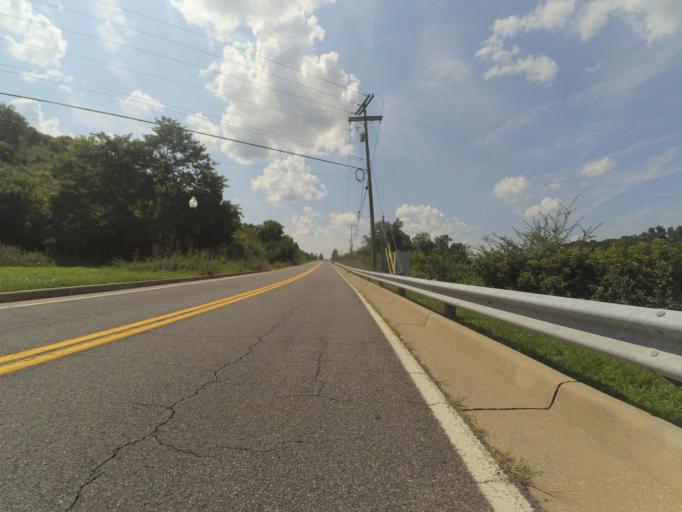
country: US
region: West Virginia
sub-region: Cabell County
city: Huntington
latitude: 38.3961
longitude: -82.4191
